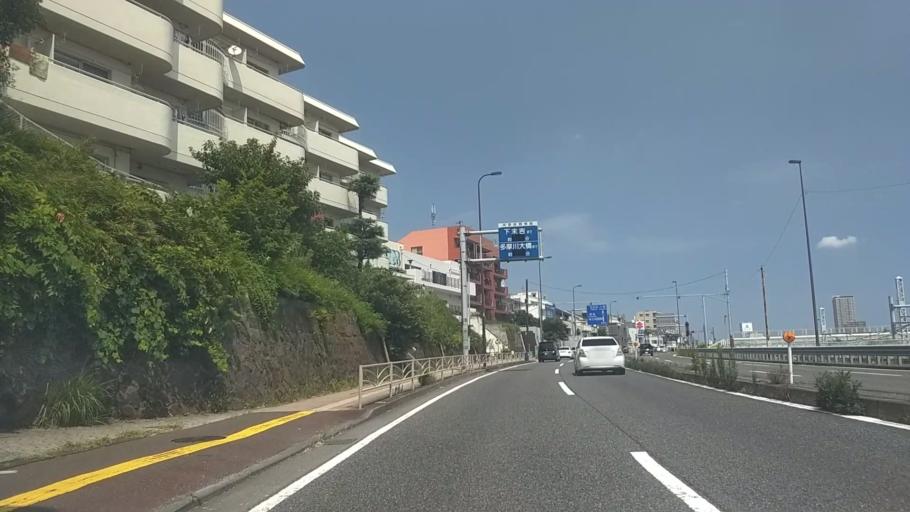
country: JP
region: Kanagawa
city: Yokohama
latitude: 35.4824
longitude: 139.6369
